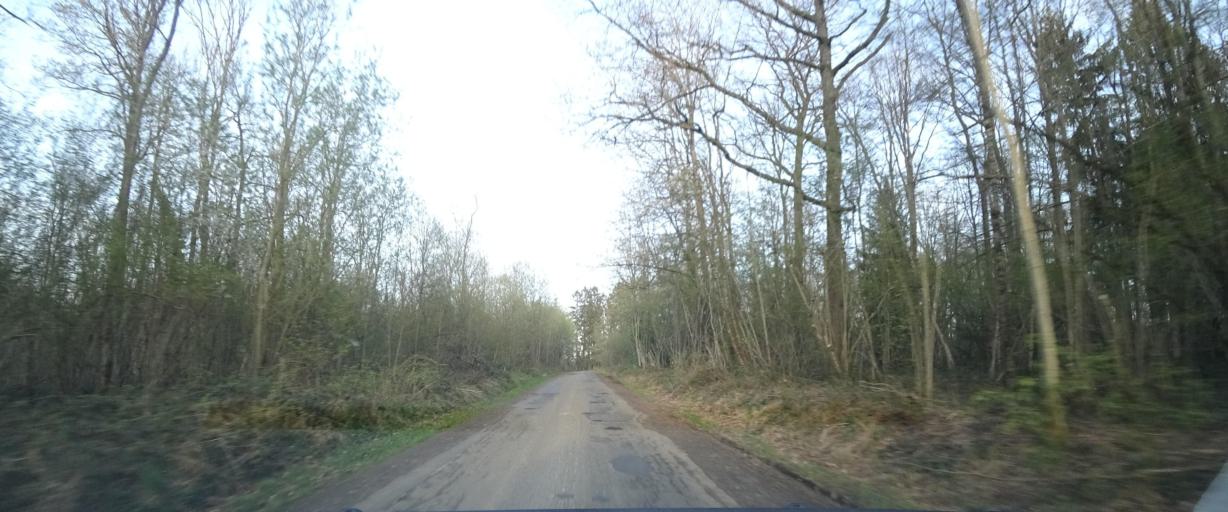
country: BE
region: Wallonia
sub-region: Province de Namur
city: Hamois
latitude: 50.3100
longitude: 5.1741
